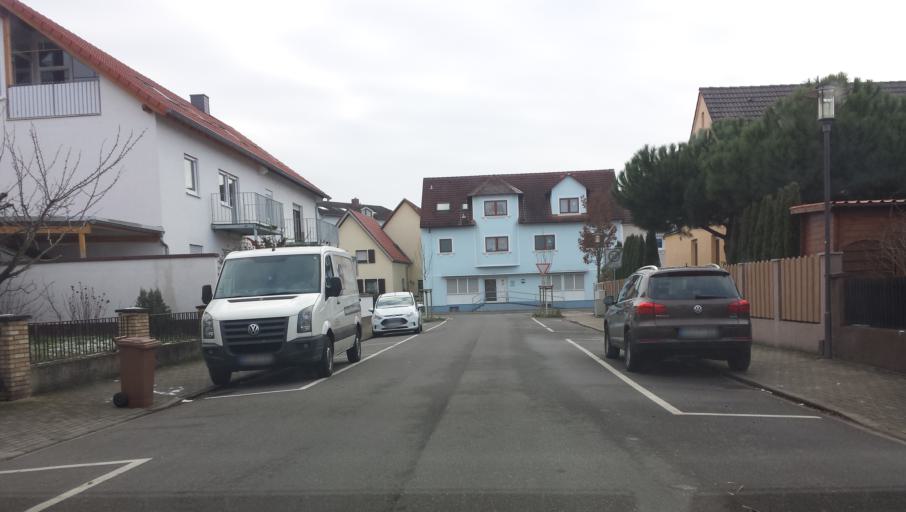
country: DE
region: Baden-Wuerttemberg
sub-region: Karlsruhe Region
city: Bruhl
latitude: 49.4091
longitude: 8.5231
